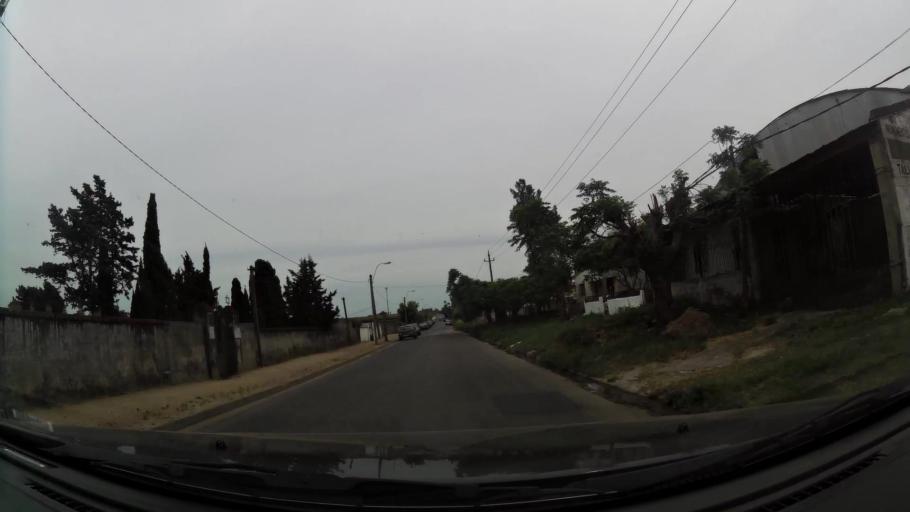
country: UY
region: Canelones
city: La Paz
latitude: -34.7524
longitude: -56.2278
